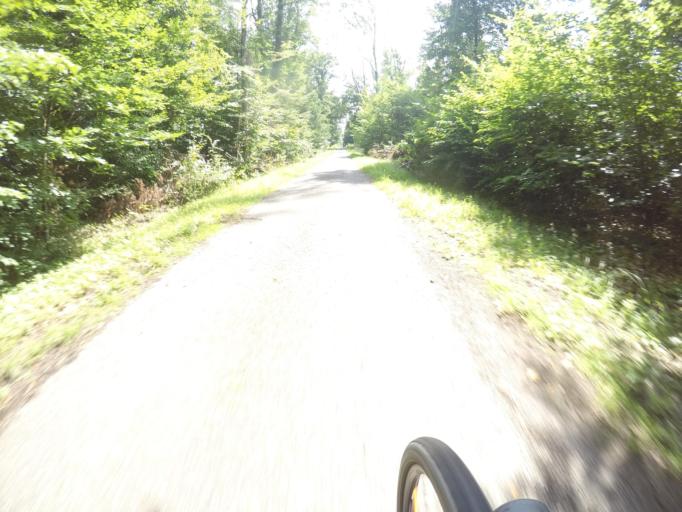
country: DE
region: Baden-Wuerttemberg
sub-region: Karlsruhe Region
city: Kronau
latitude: 49.2139
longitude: 8.5854
